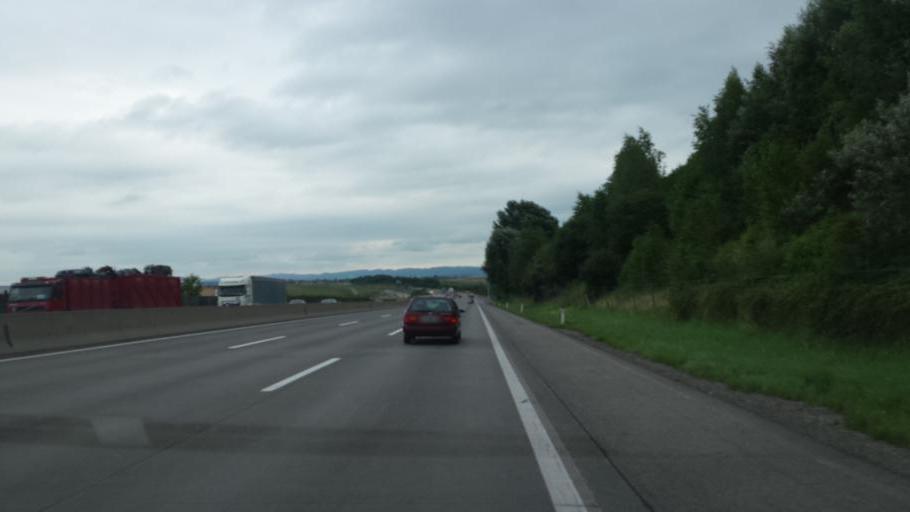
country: AT
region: Lower Austria
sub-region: Politischer Bezirk Sankt Polten
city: Sankt Margarethen an der Sierning
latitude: 48.1743
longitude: 15.4680
